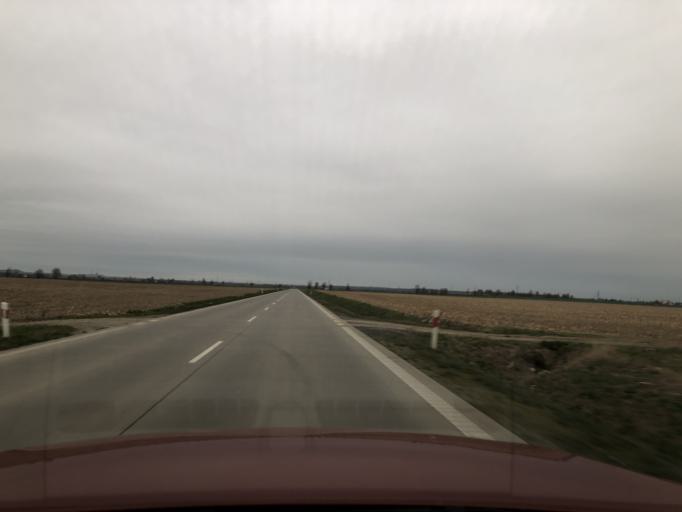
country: PL
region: Lower Silesian Voivodeship
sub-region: Powiat swidnicki
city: Zarow
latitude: 50.9183
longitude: 16.4783
